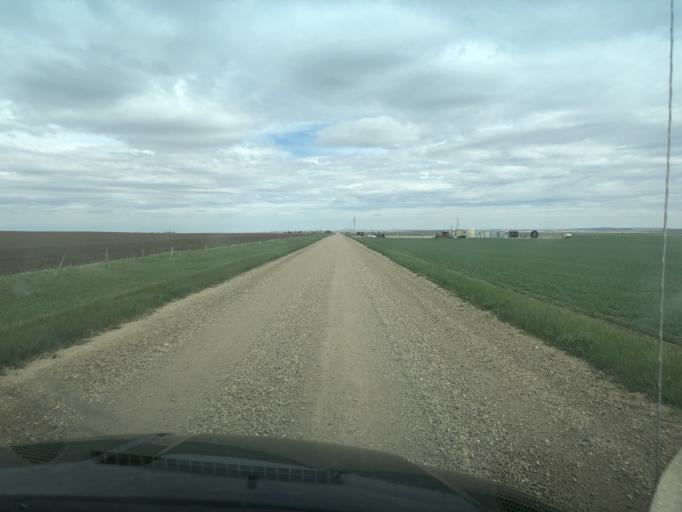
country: CA
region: Alberta
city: Vulcan
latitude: 50.3702
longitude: -113.3231
